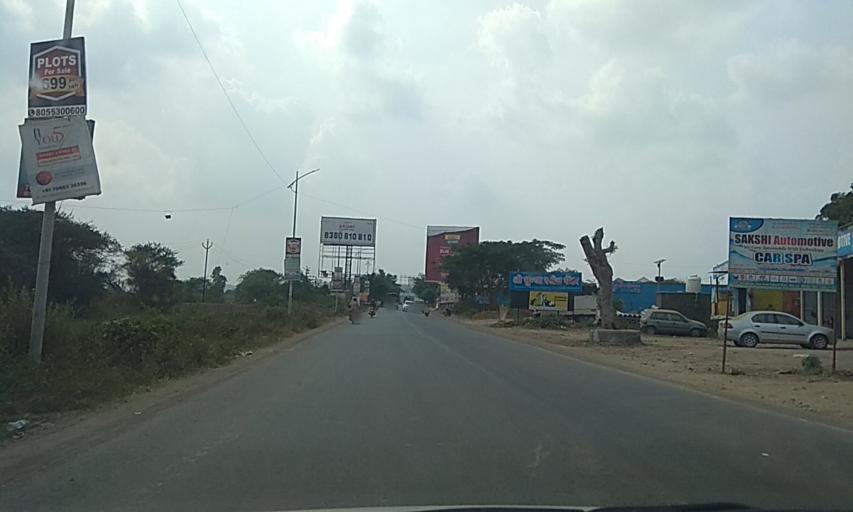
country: IN
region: Maharashtra
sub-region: Pune Division
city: Pimpri
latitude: 18.5799
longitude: 73.7191
